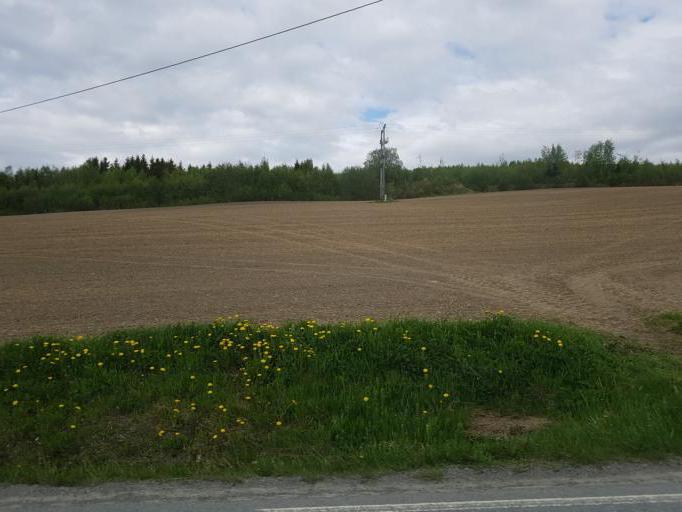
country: NO
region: Nord-Trondelag
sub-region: Levanger
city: Skogn
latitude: 63.6885
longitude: 11.2263
